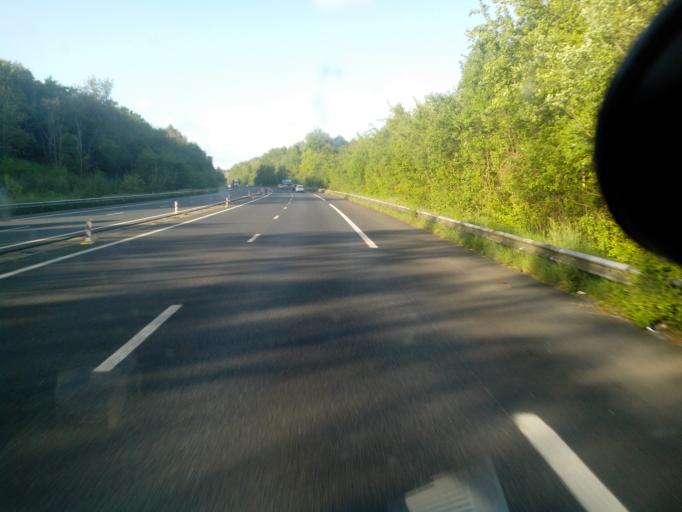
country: FR
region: Haute-Normandie
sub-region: Departement de la Seine-Maritime
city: Saint-Saens
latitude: 49.6632
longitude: 1.3074
